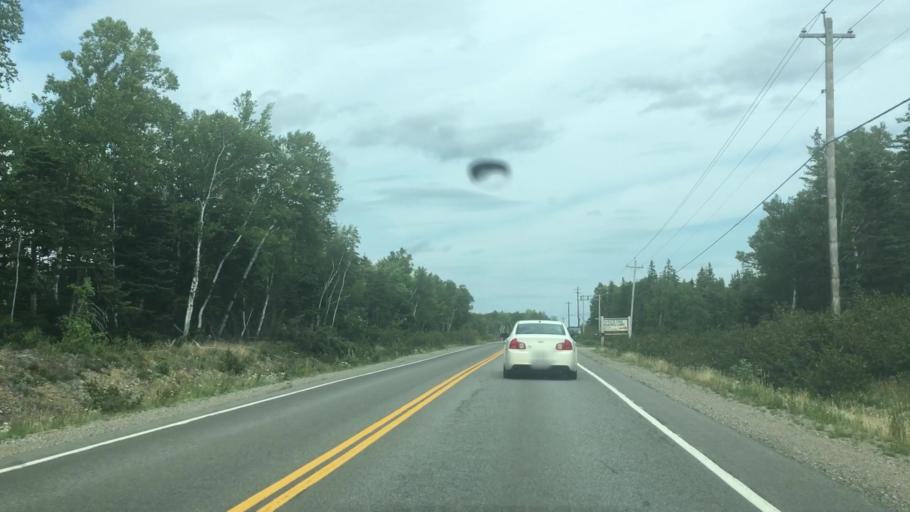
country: CA
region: Nova Scotia
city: Sydney Mines
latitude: 46.5193
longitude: -60.4237
